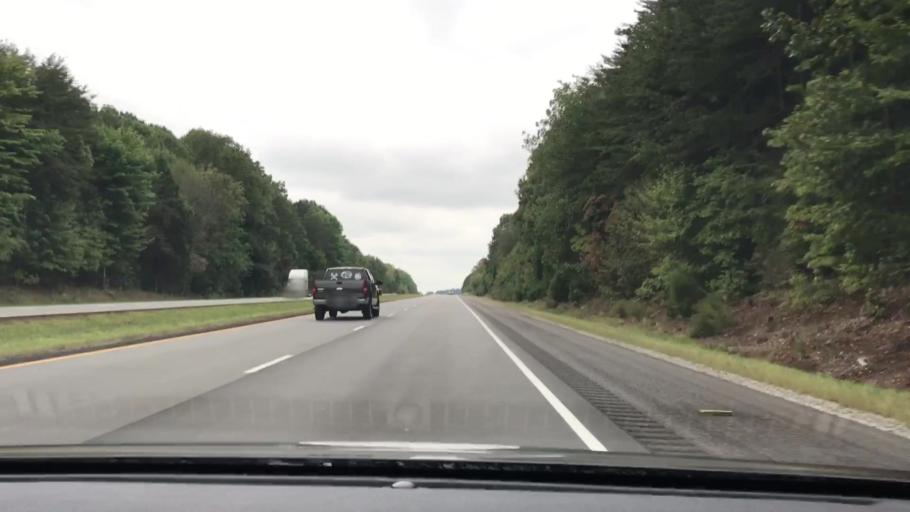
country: US
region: Kentucky
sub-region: Barren County
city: Glasgow
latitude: 36.9972
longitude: -85.8055
